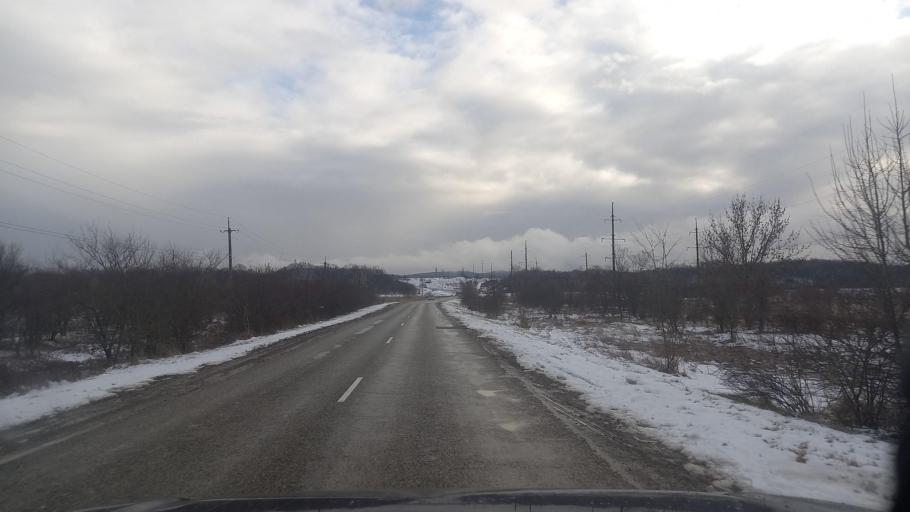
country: RU
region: Krasnodarskiy
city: Smolenskaya
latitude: 44.7764
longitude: 38.8139
